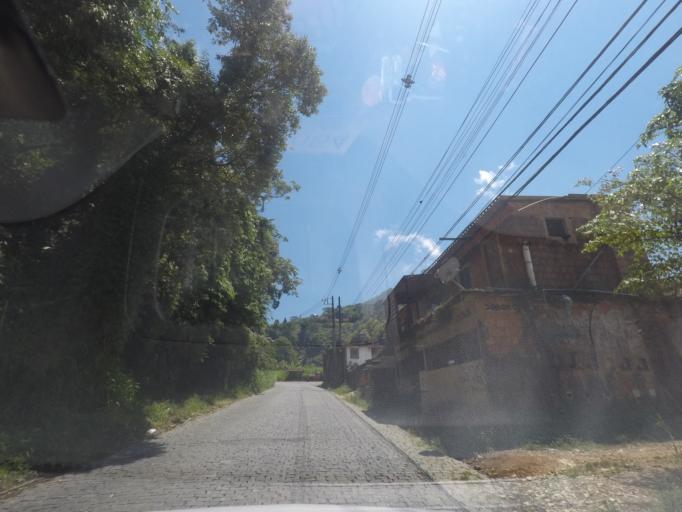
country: BR
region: Rio de Janeiro
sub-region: Petropolis
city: Petropolis
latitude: -22.5366
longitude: -43.1750
